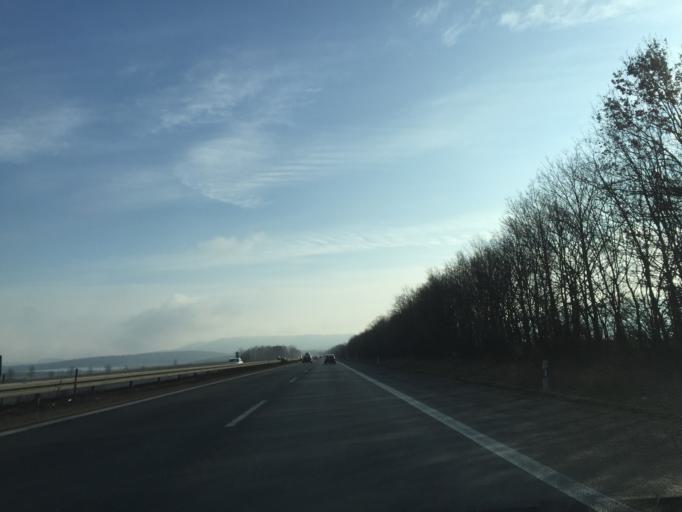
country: DE
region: Bavaria
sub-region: Regierungsbezirk Unterfranken
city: Wiesentheid
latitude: 49.7746
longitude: 10.3570
